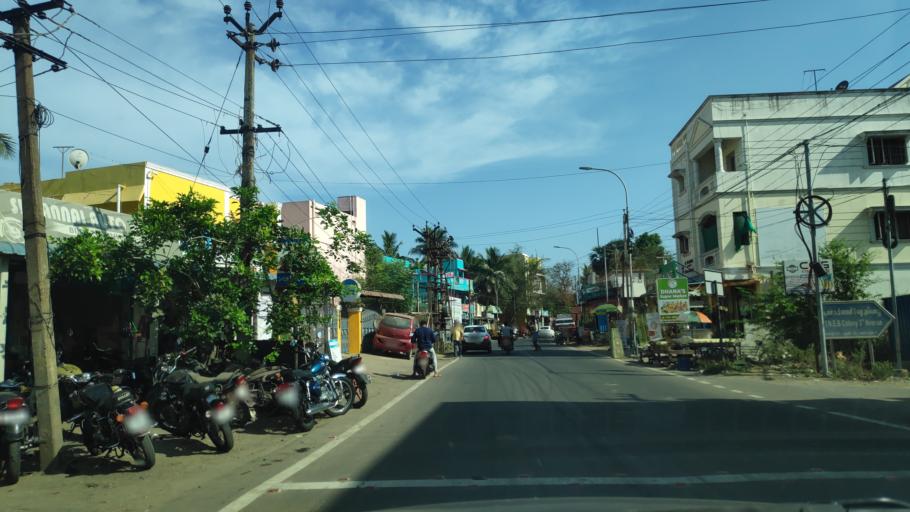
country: IN
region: Tamil Nadu
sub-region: Thiruvallur
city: Ambattur
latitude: 13.1197
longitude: 80.1688
